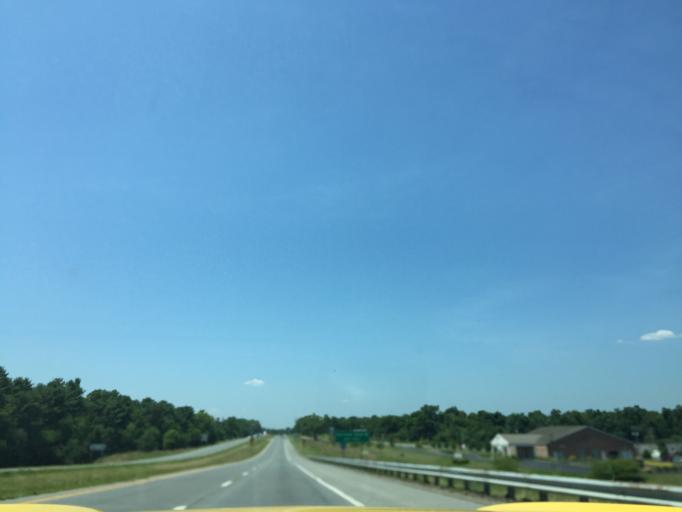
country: US
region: West Virginia
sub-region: Jefferson County
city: Bolivar
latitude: 39.3075
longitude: -77.8028
